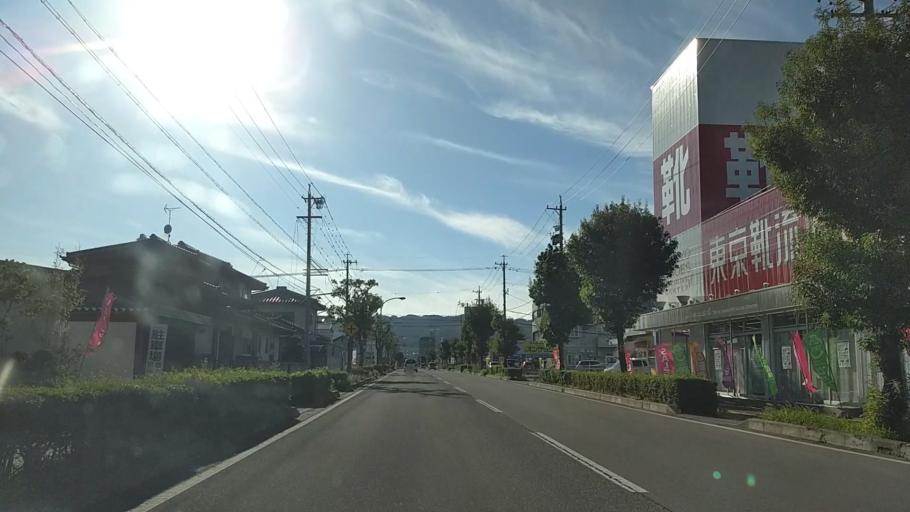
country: JP
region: Nagano
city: Nagano-shi
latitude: 36.5818
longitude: 138.1591
